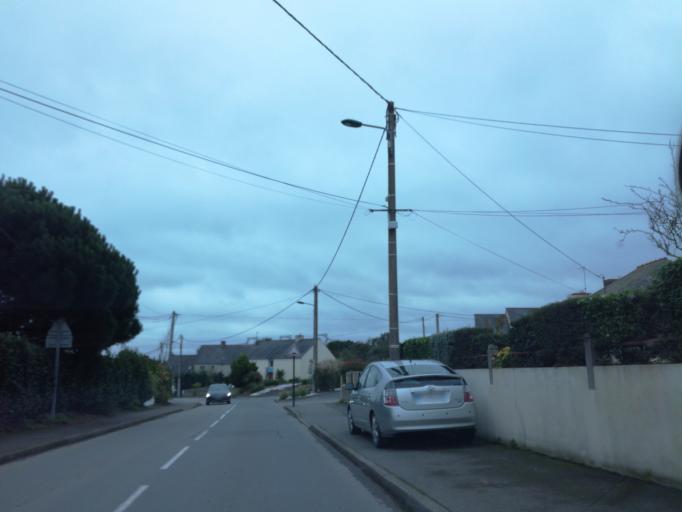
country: FR
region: Brittany
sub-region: Departement d'Ille-et-Vilaine
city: La Richardais
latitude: 48.6105
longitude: -2.0445
